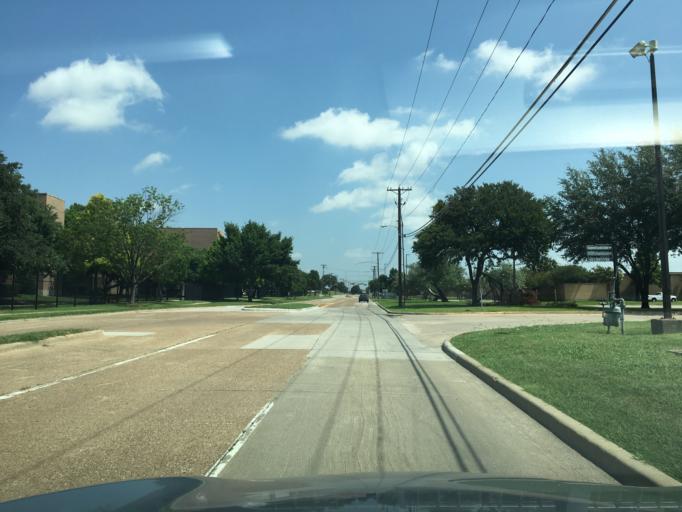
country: US
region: Texas
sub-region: Dallas County
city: Richardson
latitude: 32.9282
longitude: -96.7490
